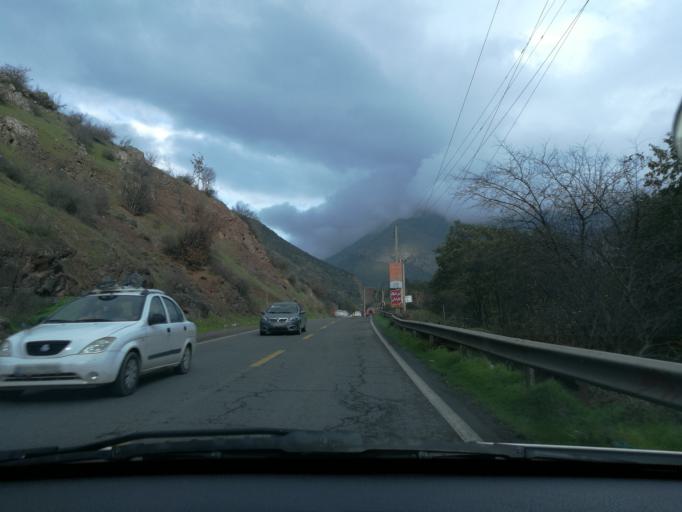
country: IR
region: Mazandaran
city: Chalus
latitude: 36.3740
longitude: 51.2698
